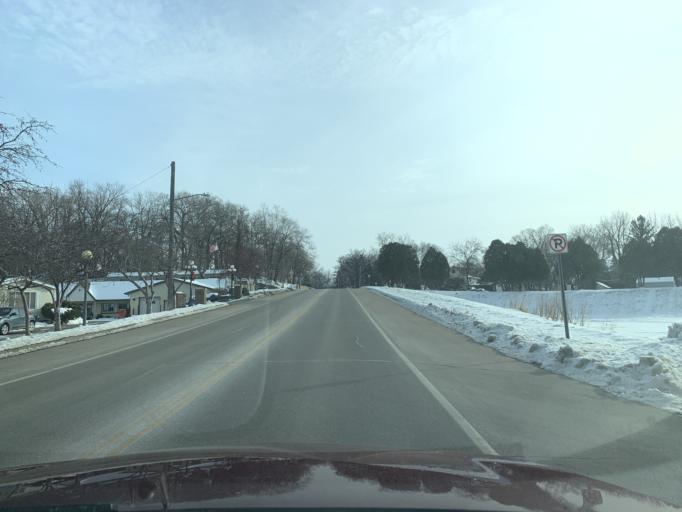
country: US
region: Minnesota
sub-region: Washington County
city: Saint Paul Park
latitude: 44.8470
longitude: -92.9882
